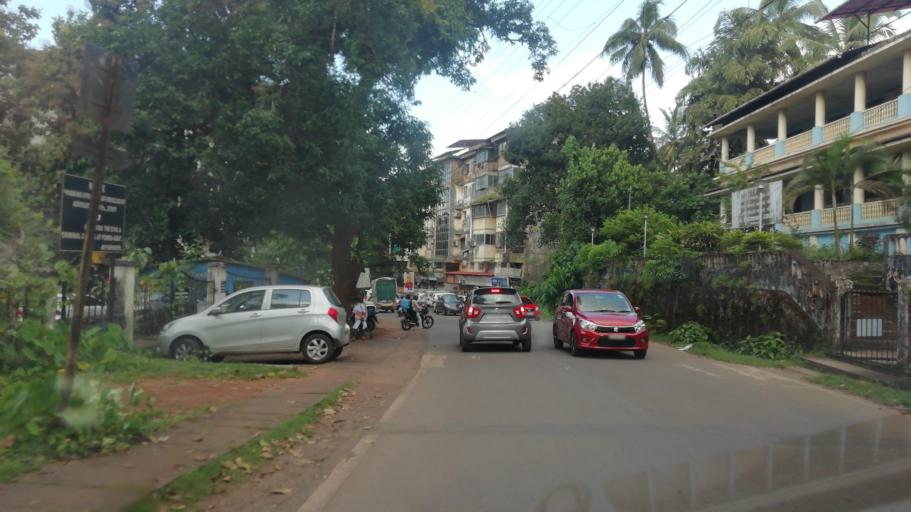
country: IN
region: Goa
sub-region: North Goa
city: Queula
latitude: 15.3930
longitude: 74.0007
